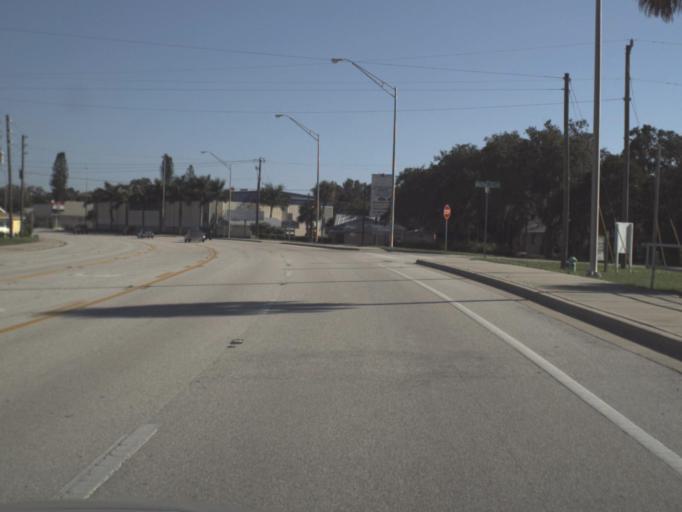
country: US
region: Florida
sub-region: Sarasota County
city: Englewood
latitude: 26.9473
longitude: -82.3532
